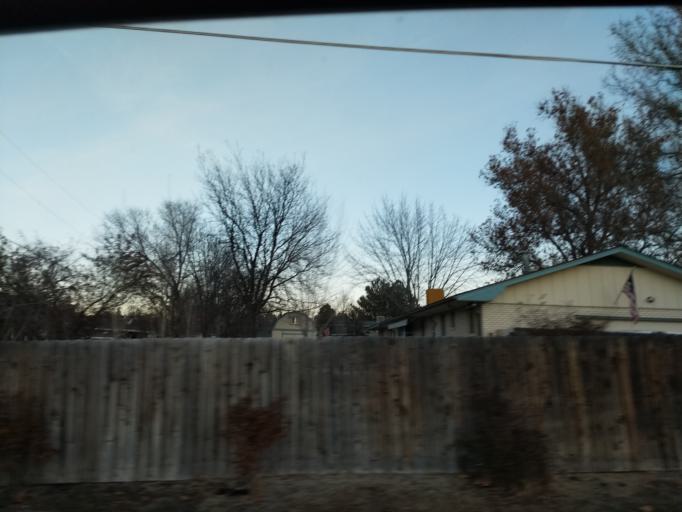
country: US
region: Colorado
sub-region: Mesa County
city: Grand Junction
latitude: 39.1080
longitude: -108.5616
